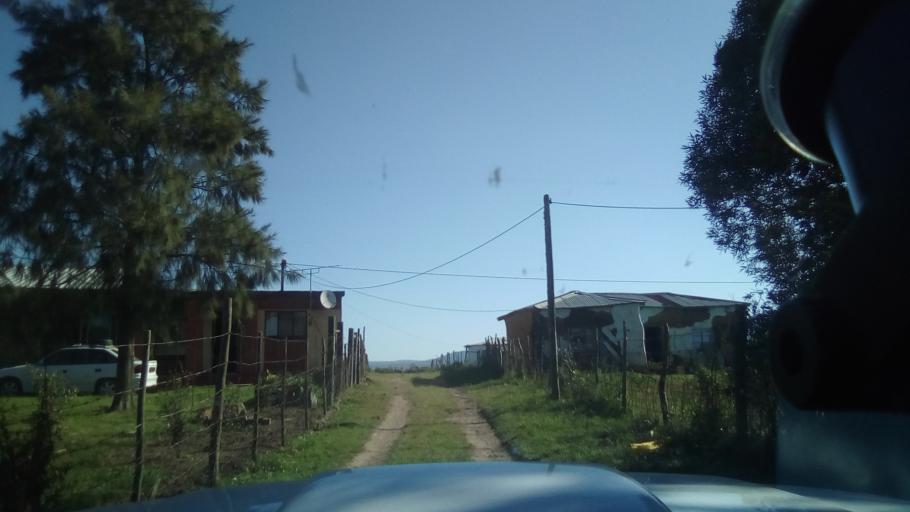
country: ZA
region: Eastern Cape
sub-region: Buffalo City Metropolitan Municipality
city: Bhisho
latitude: -32.8015
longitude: 27.3394
